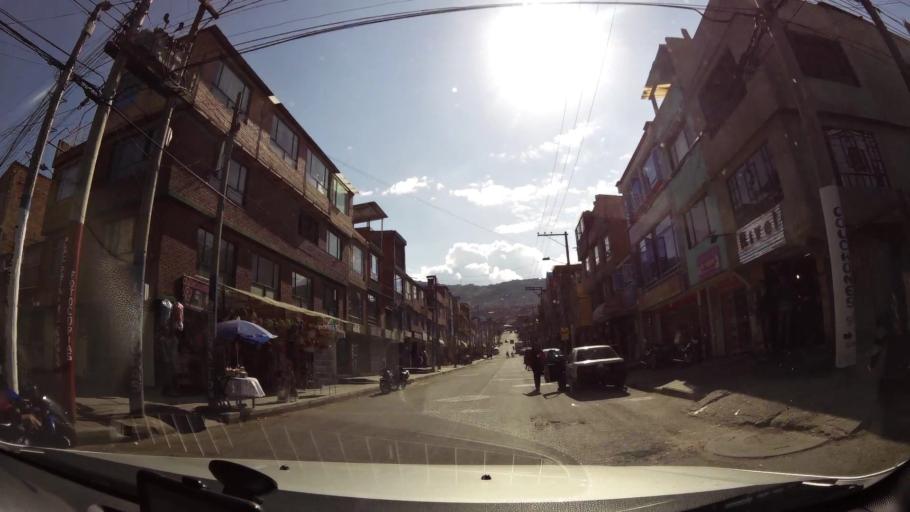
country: CO
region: Cundinamarca
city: Soacha
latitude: 4.5468
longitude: -74.1386
